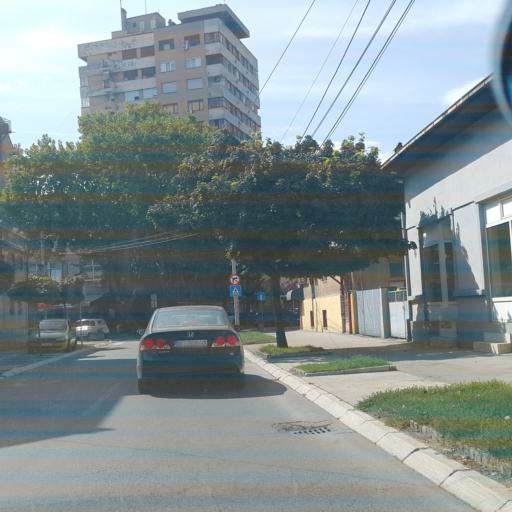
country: RS
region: Central Serbia
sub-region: Nisavski Okrug
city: Nis
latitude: 43.3226
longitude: 21.8990
